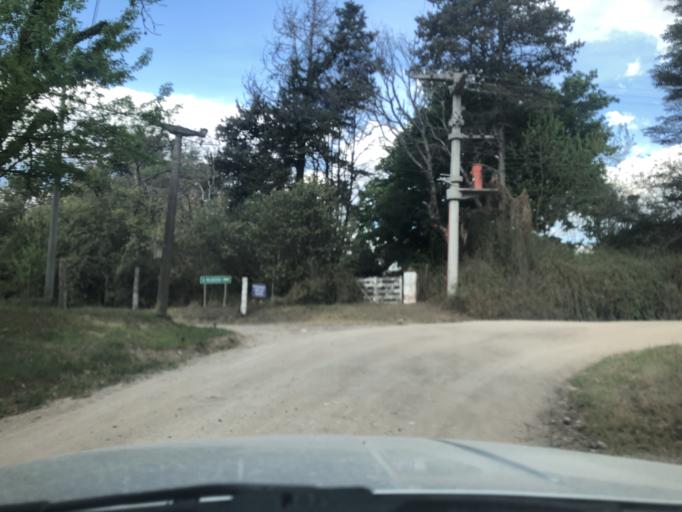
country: AR
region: Cordoba
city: La Granja
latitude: -31.0040
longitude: -64.2493
